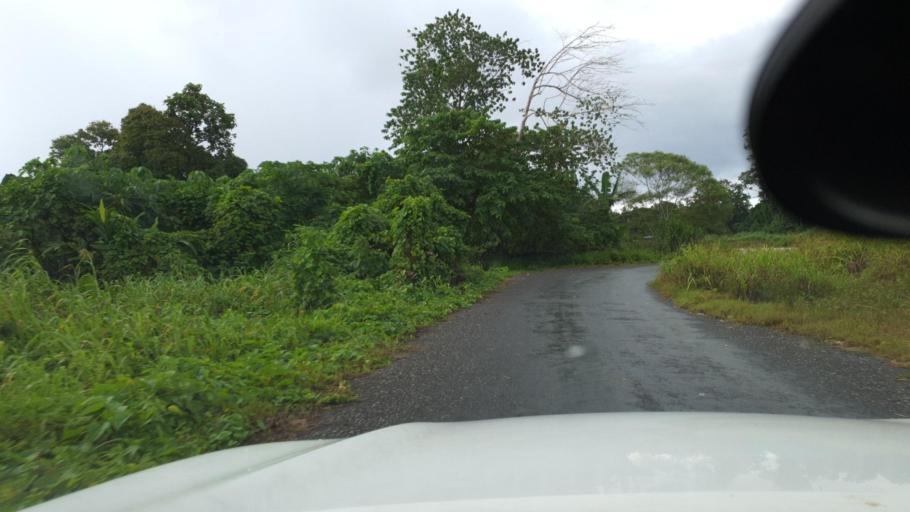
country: SB
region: Guadalcanal
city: Honiara
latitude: -9.4662
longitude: 160.3591
